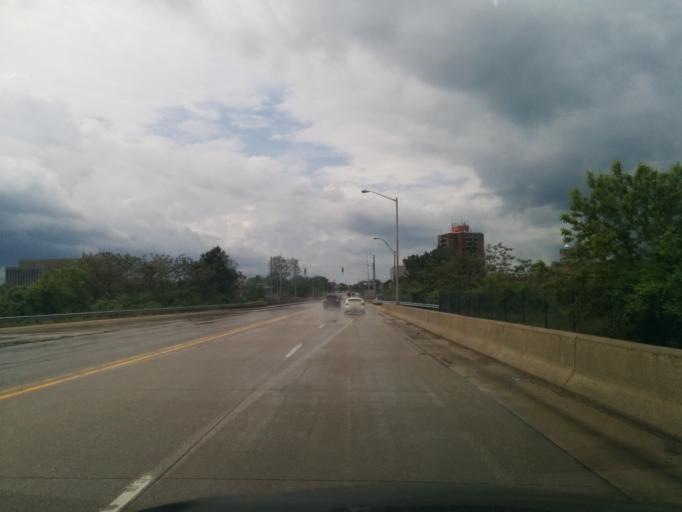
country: US
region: Michigan
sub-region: Berrien County
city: Saint Joseph
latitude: 42.1137
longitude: -86.4768
